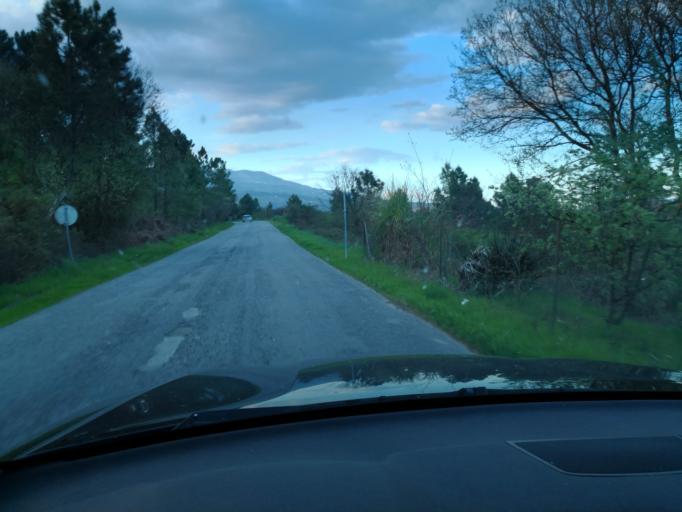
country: PT
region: Vila Real
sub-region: Vila Real
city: Vila Real
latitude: 41.3024
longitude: -7.7632
